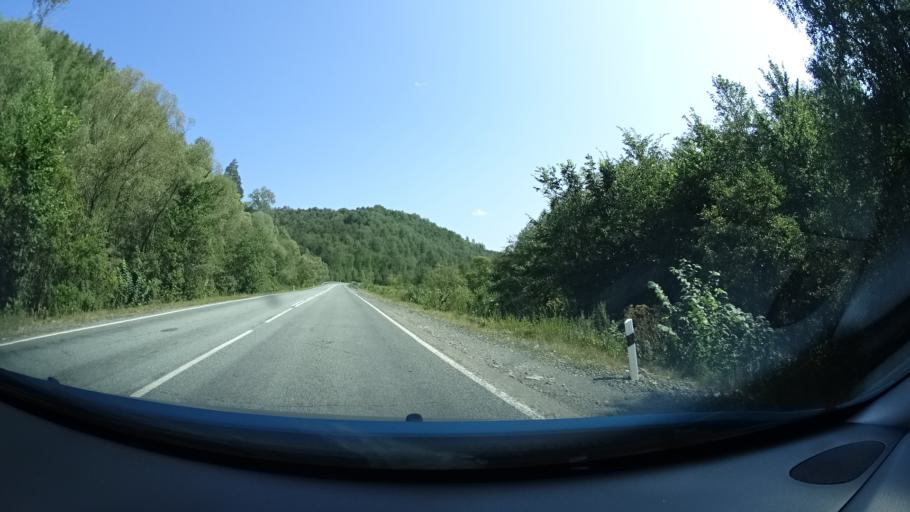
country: RU
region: Bashkortostan
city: Inzer
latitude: 54.3179
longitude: 57.1800
